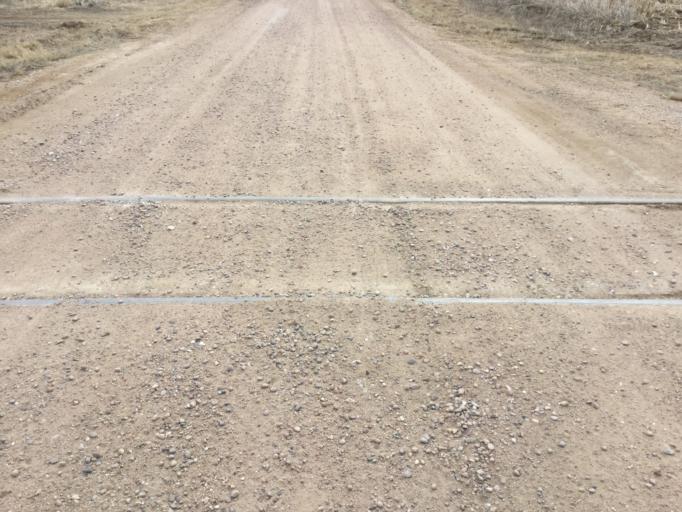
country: US
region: Kansas
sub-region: Lane County
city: Dighton
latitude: 38.4834
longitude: -100.6129
